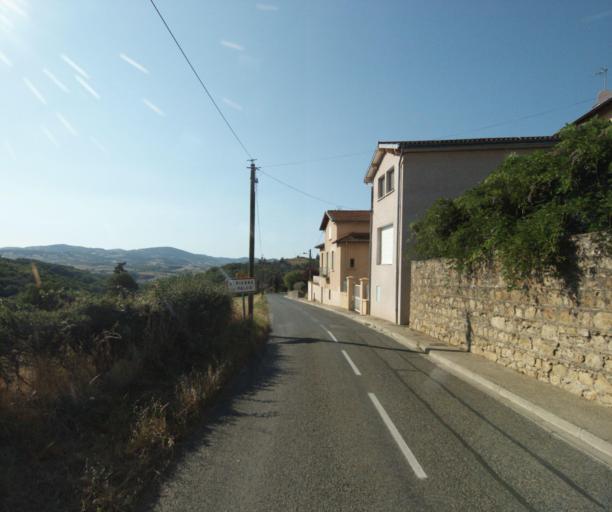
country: FR
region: Rhone-Alpes
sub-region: Departement du Rhone
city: Saint-Pierre-la-Palud
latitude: 45.7852
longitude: 4.6151
